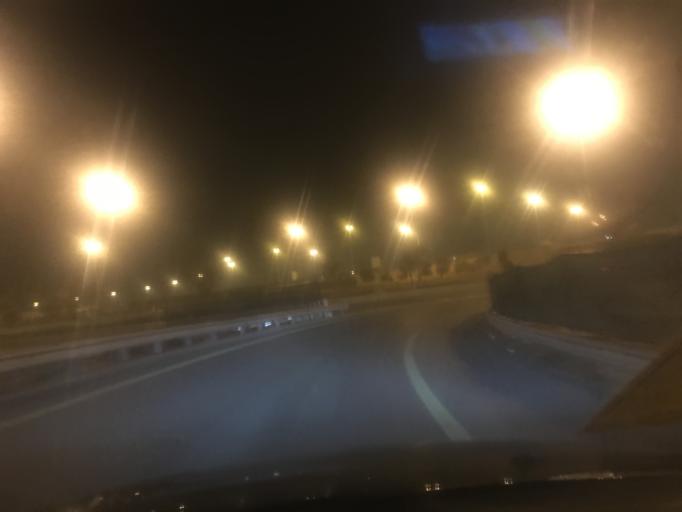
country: SA
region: Ar Riyad
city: Riyadh
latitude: 24.7982
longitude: 46.5638
